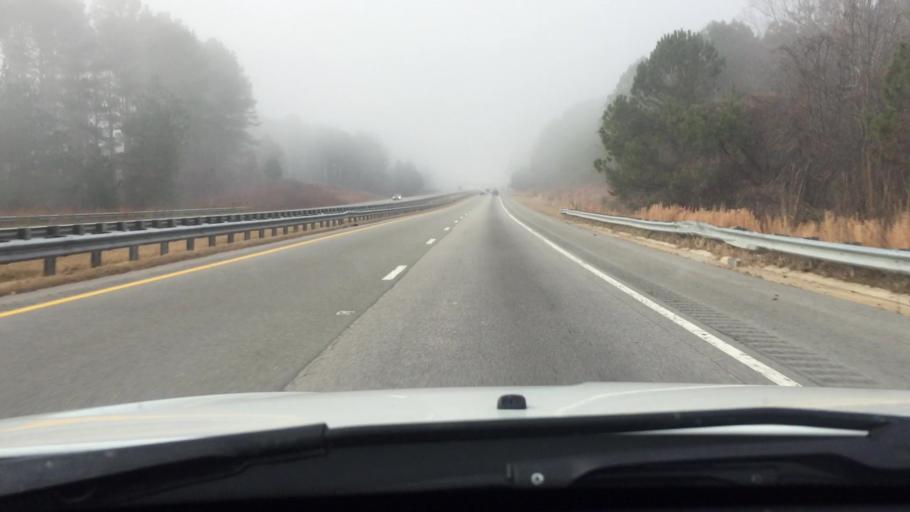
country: US
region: North Carolina
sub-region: Wake County
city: Holly Springs
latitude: 35.6727
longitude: -78.9213
